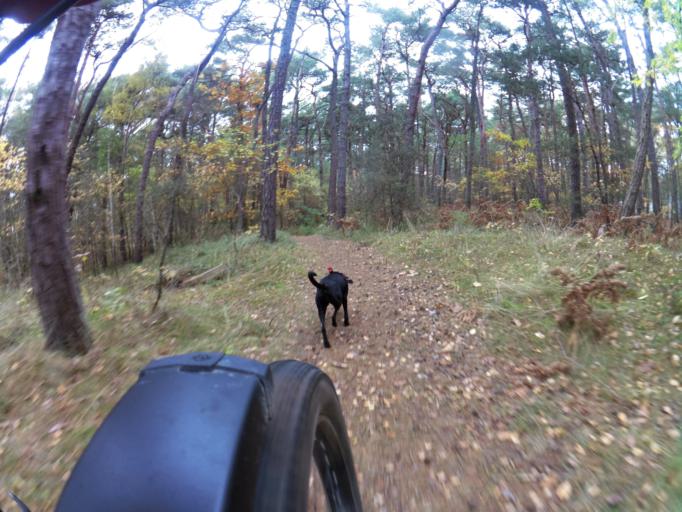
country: PL
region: Pomeranian Voivodeship
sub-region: Powiat pucki
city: Jastarnia
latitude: 54.6908
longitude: 18.6964
